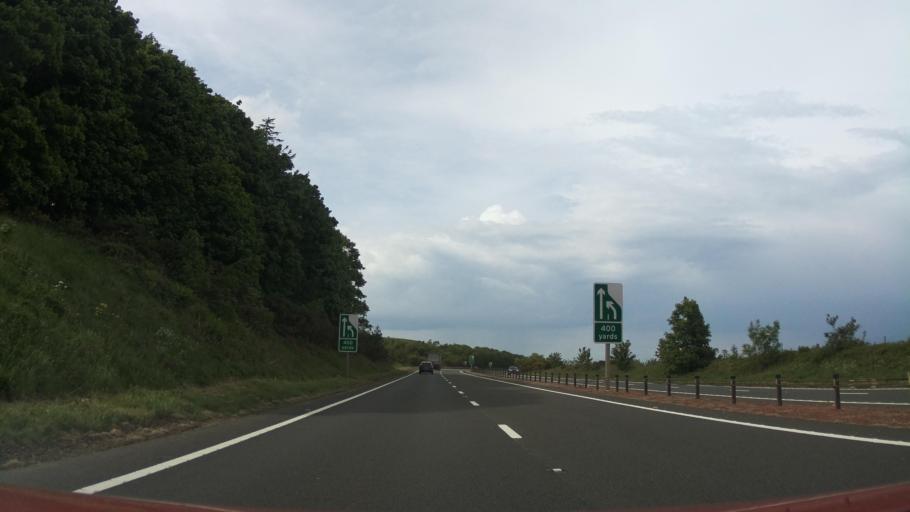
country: GB
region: Scotland
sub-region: The Scottish Borders
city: Duns
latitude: 55.9115
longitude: -2.3389
